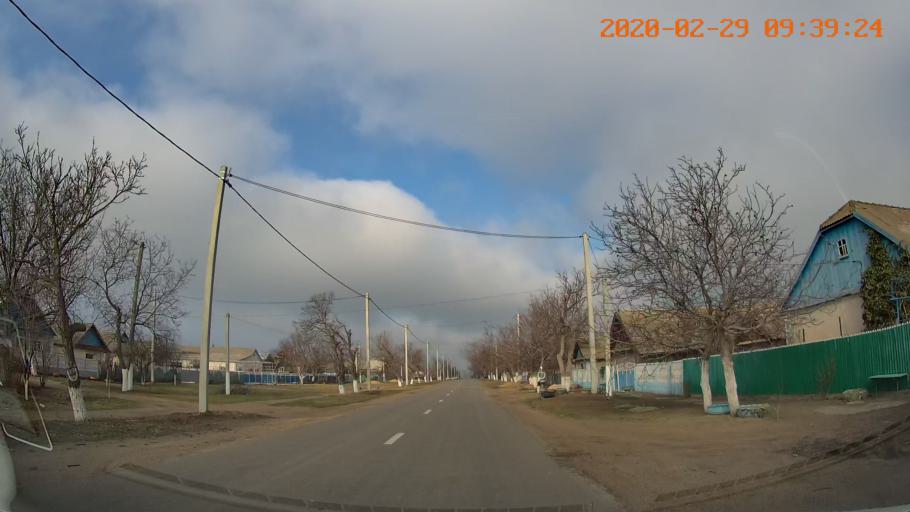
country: MD
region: Telenesti
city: Crasnoe
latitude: 46.6353
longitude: 29.8553
